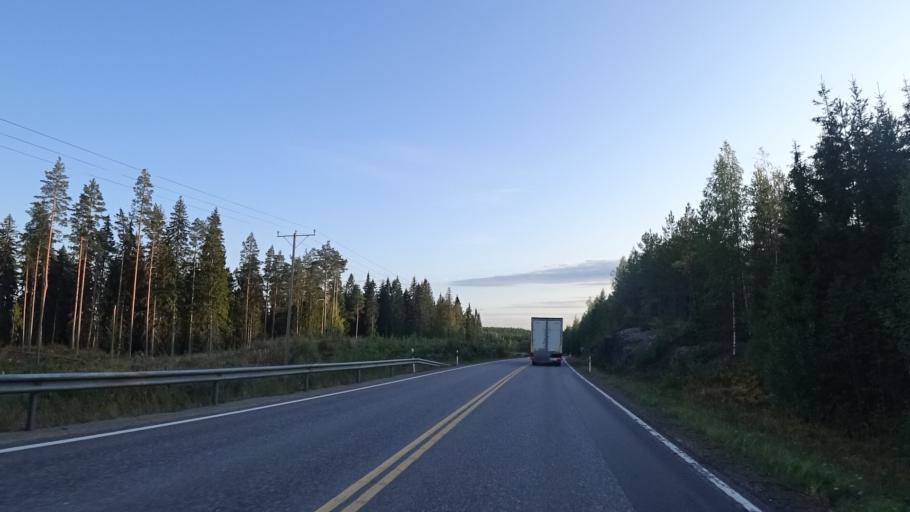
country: FI
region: South Karelia
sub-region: Lappeenranta
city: Ylaemaa
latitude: 60.7778
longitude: 27.9895
